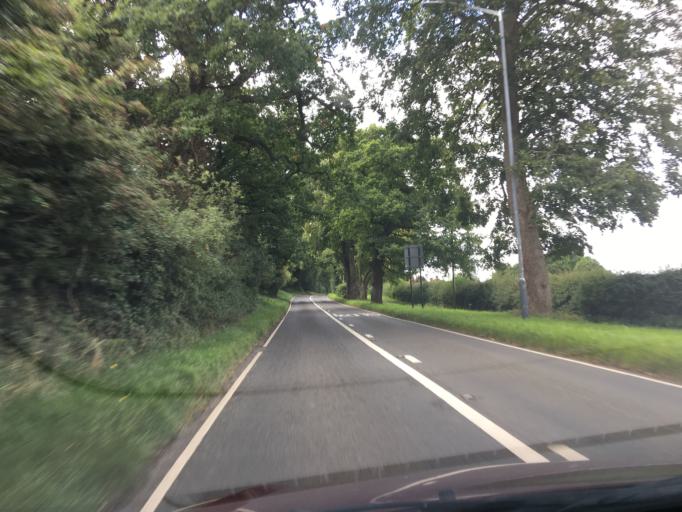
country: GB
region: England
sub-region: Warwickshire
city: Royal Leamington Spa
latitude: 52.3189
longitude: -1.5317
